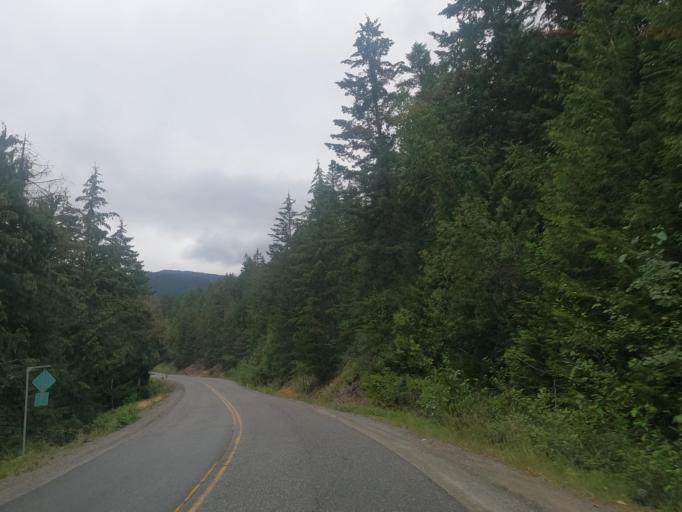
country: CA
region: British Columbia
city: Pemberton
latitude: 50.3032
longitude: -122.5741
